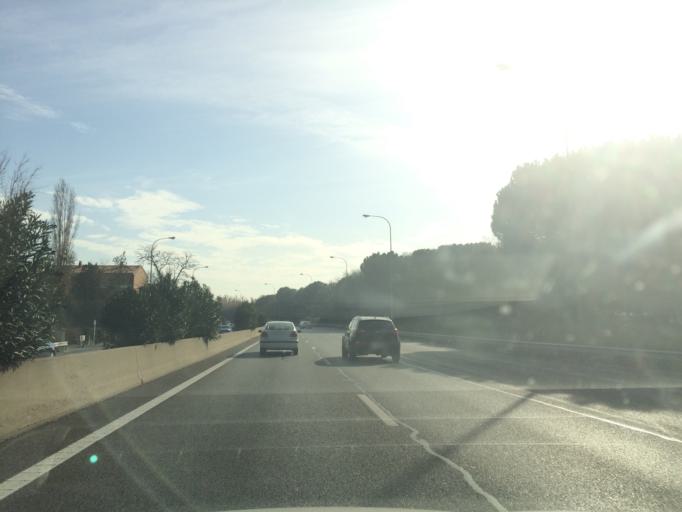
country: ES
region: Madrid
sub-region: Provincia de Madrid
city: Moncloa-Aravaca
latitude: 40.4315
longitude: -3.7374
